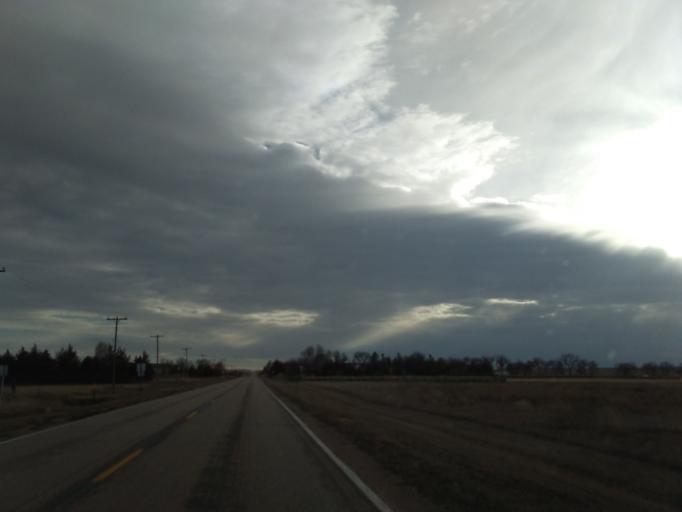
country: US
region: Nebraska
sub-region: Morrill County
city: Bridgeport
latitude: 41.6548
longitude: -103.0995
